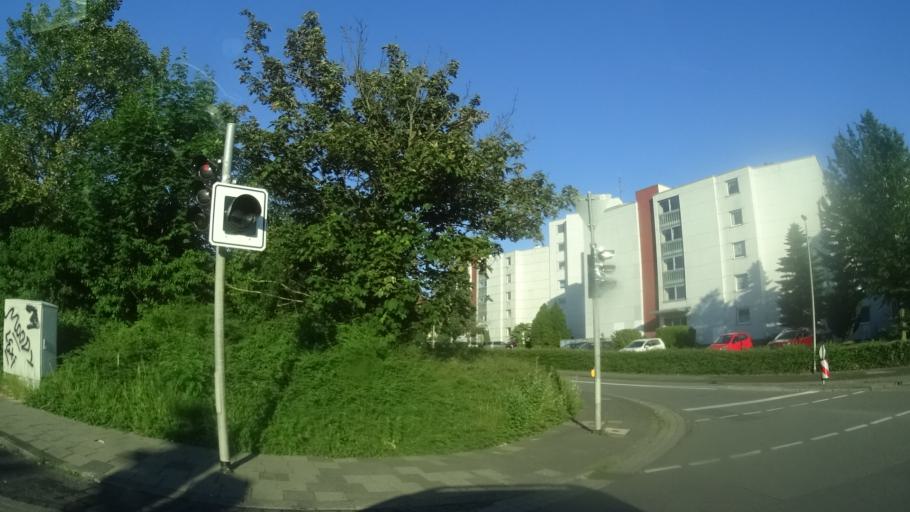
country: DE
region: Lower Saxony
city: Hildesheim
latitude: 52.1451
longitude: 9.9629
